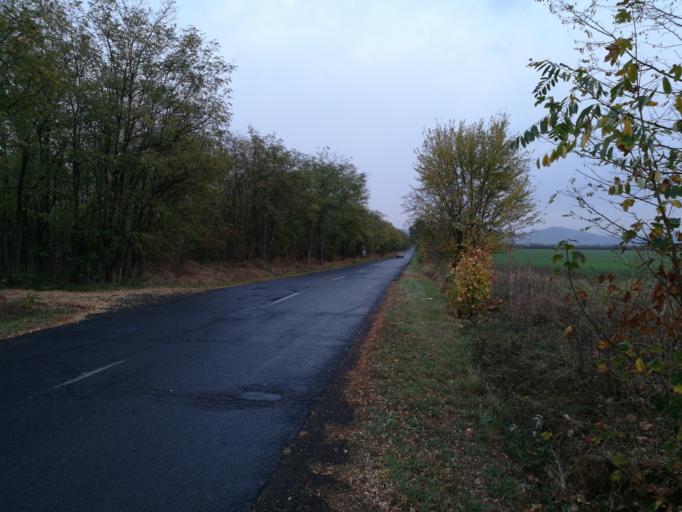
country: HU
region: Nograd
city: Palotas
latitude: 47.8221
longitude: 19.5989
